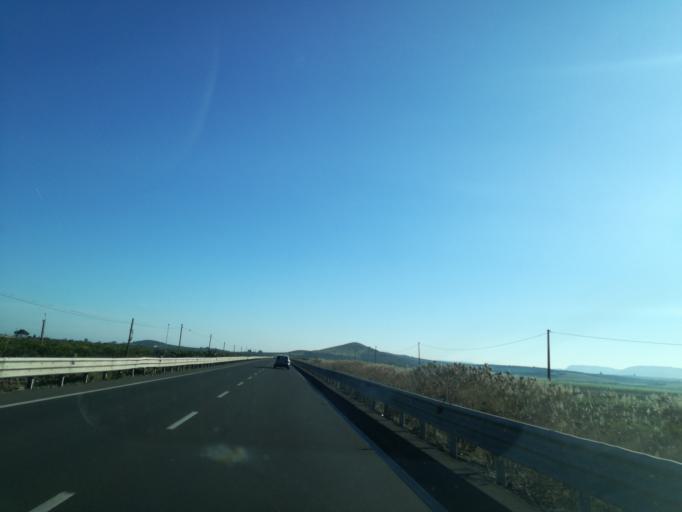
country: IT
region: Sicily
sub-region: Catania
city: Palagonia
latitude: 37.3787
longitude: 14.7794
